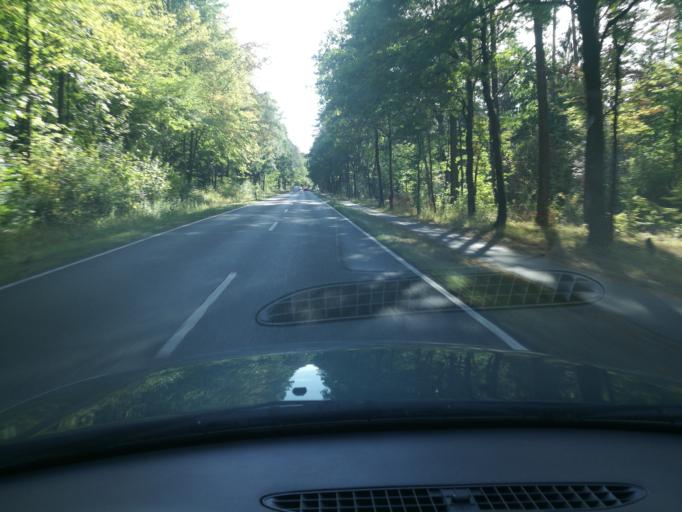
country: DE
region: Bavaria
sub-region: Regierungsbezirk Mittelfranken
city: Kalchreuth
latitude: 49.5455
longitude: 11.1018
